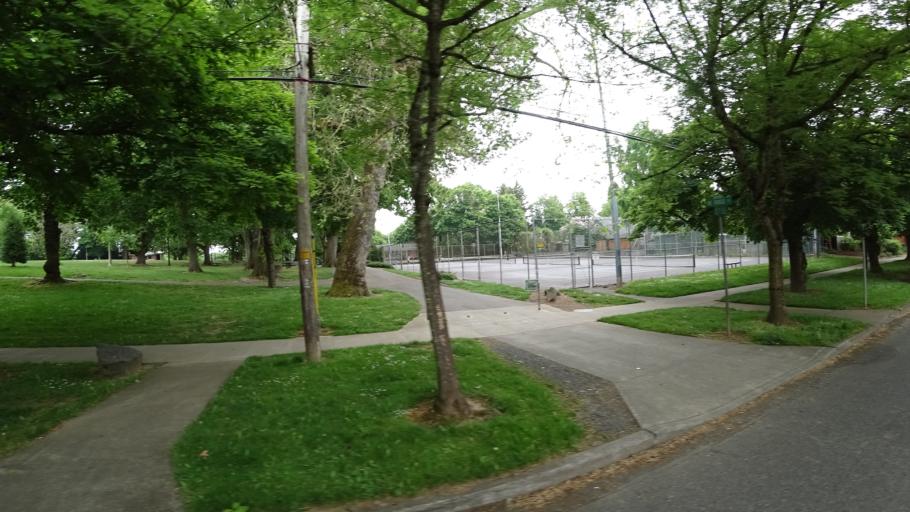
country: US
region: Oregon
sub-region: Multnomah County
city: Portland
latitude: 45.5464
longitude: -122.6586
